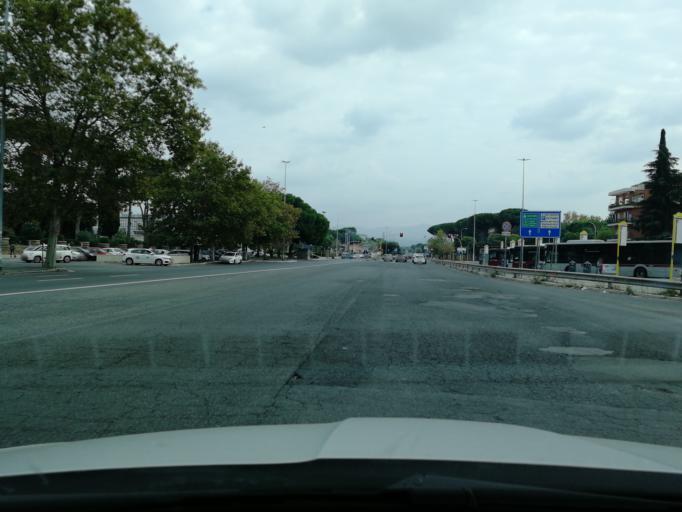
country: IT
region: Latium
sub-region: Citta metropolitana di Roma Capitale
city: Ciampino
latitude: 41.8534
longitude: 12.5682
